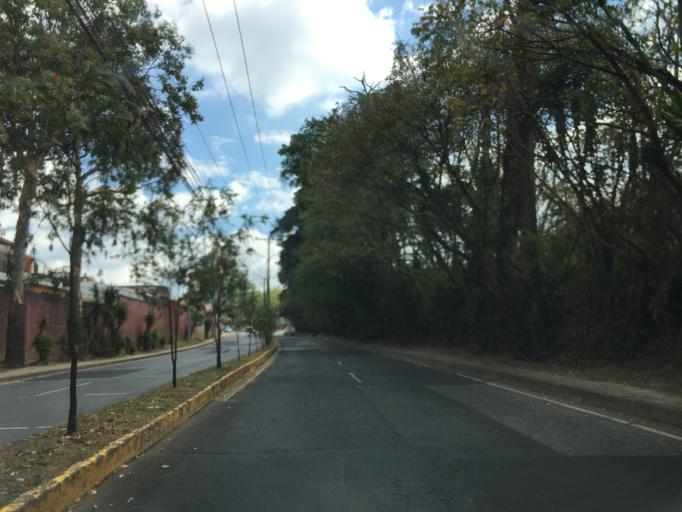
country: GT
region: Guatemala
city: Santa Catarina Pinula
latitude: 14.6100
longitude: -90.4716
